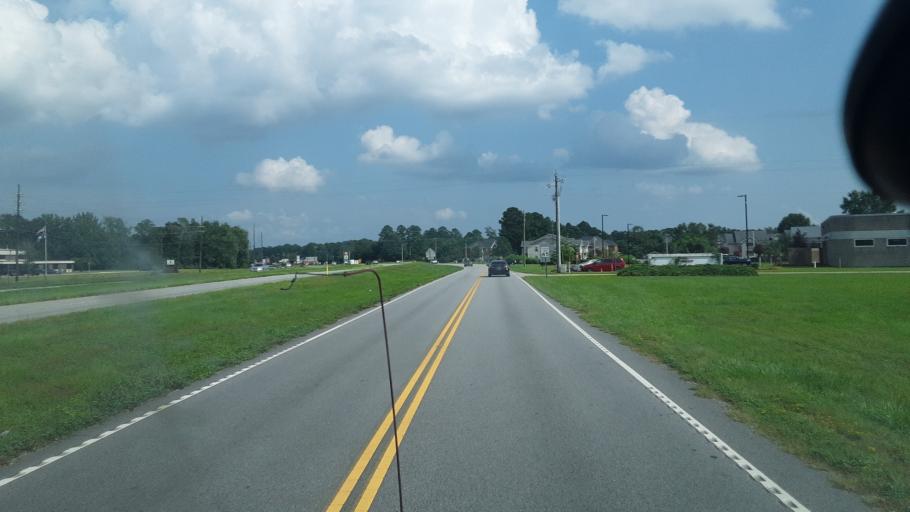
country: US
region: South Carolina
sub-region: Sumter County
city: Sumter
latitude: 33.9486
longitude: -80.3594
